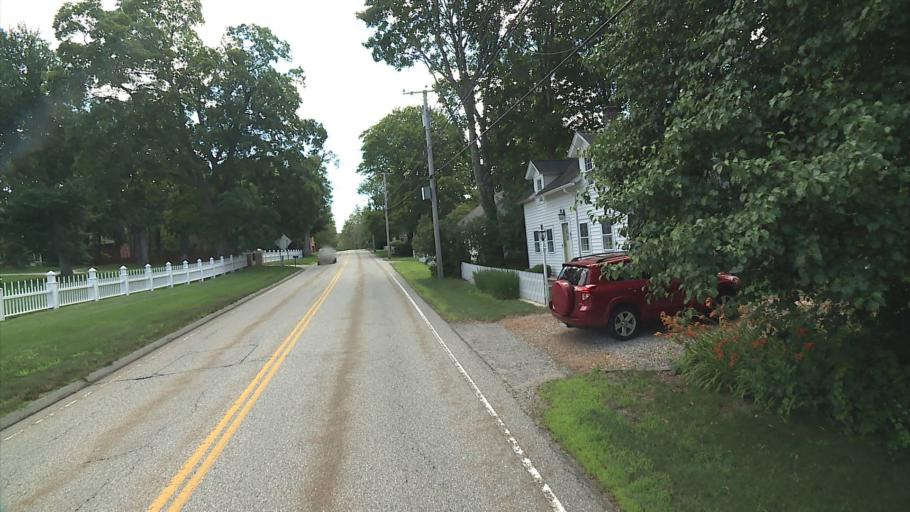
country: US
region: Connecticut
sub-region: Middlesex County
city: East Hampton
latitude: 41.5515
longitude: -72.5494
